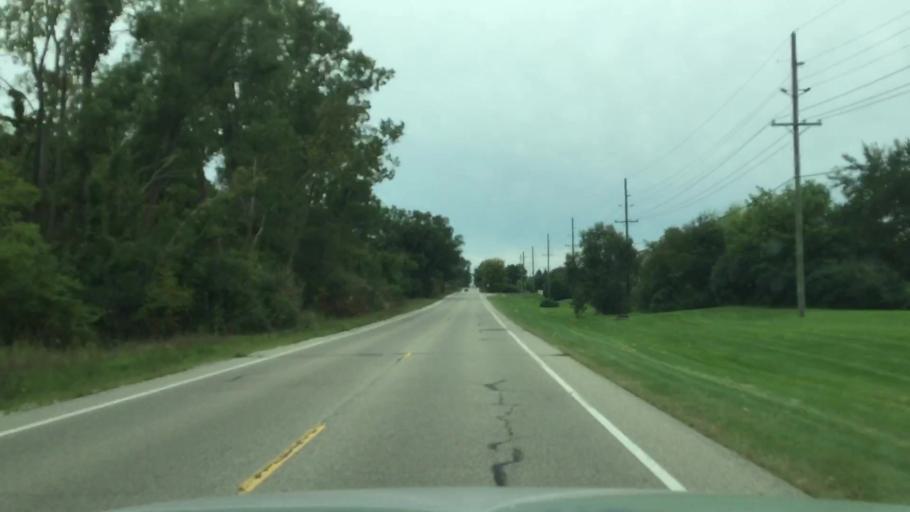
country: US
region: Michigan
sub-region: Washtenaw County
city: Ypsilanti
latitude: 42.2135
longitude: -83.6601
